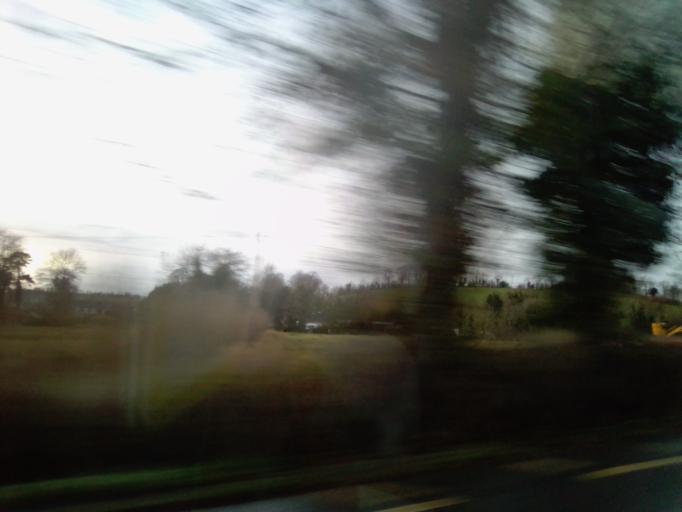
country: IE
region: Ulster
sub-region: County Monaghan
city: Monaghan
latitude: 54.3600
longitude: -6.9676
